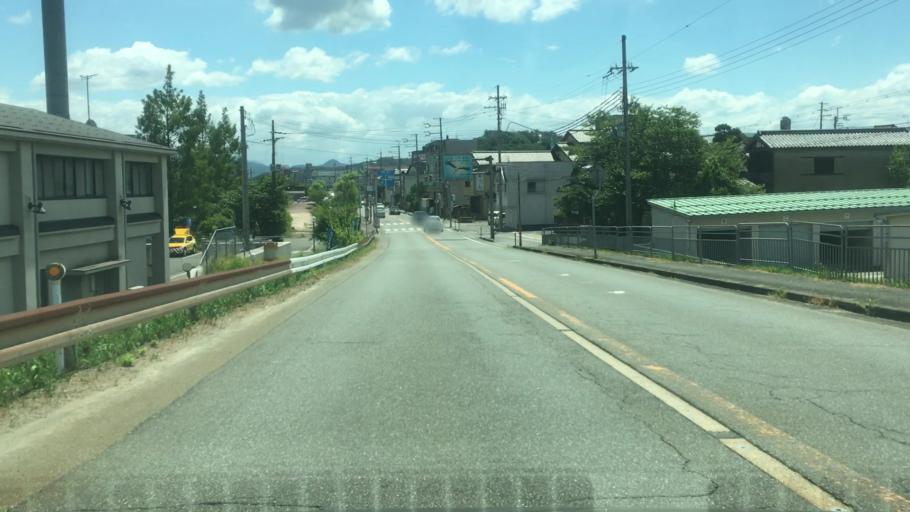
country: JP
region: Hyogo
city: Toyooka
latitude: 35.5470
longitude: 134.8261
